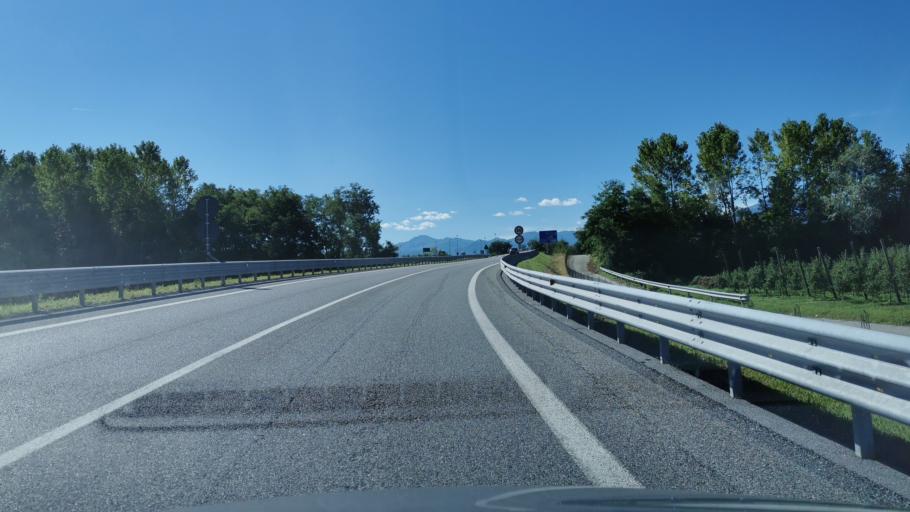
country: IT
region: Piedmont
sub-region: Provincia di Cuneo
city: Castelletto Stura
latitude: 44.4182
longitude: 7.5949
